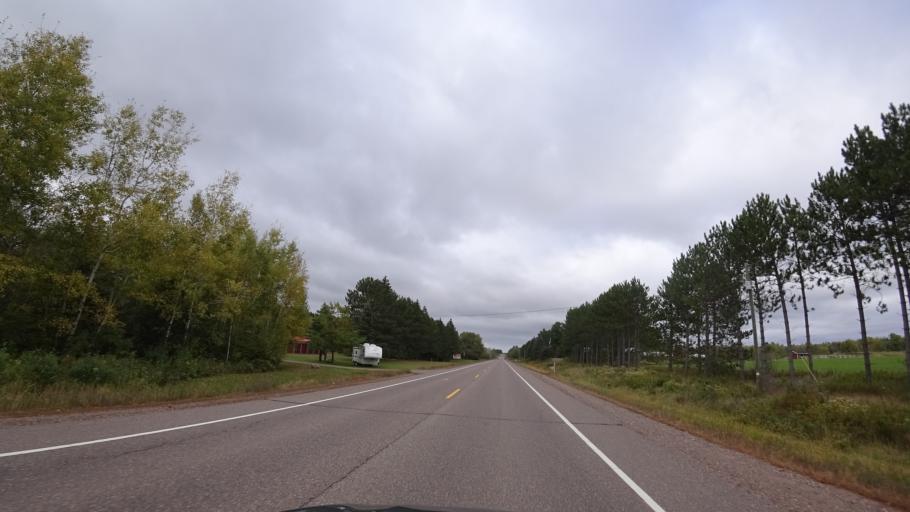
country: US
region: Wisconsin
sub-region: Rusk County
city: Ladysmith
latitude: 45.5247
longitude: -91.1115
